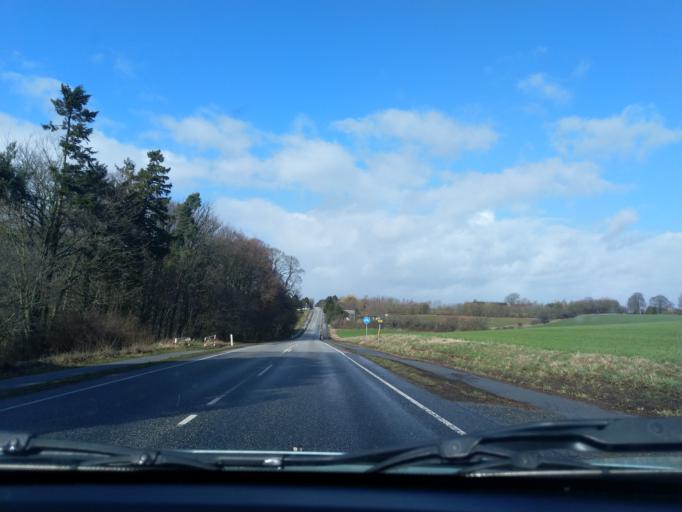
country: DK
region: Zealand
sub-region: Naestved Kommune
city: Naestved
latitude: 55.3016
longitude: 11.6911
